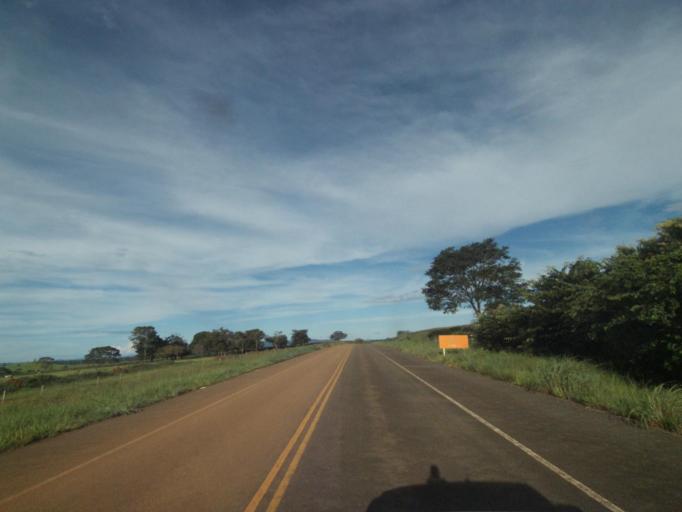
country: BR
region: Goias
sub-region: Jaragua
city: Jaragua
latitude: -15.8906
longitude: -49.4831
